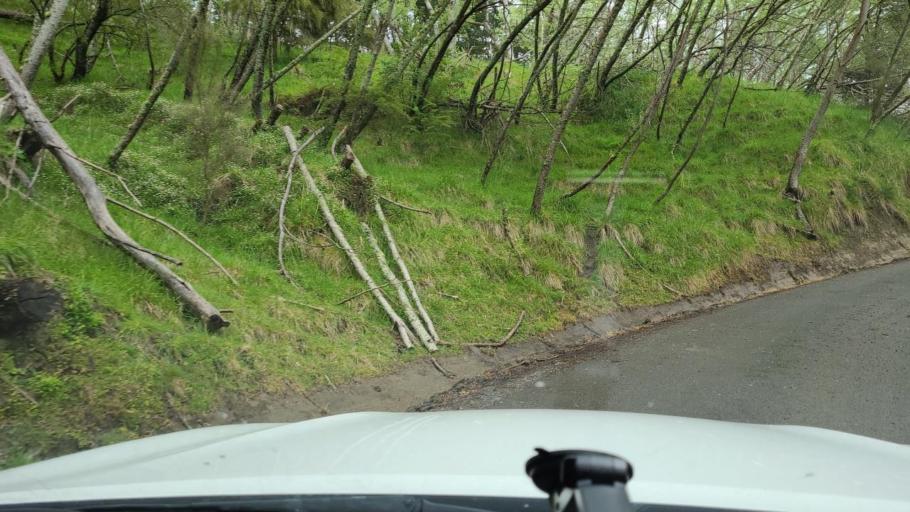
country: NZ
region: Gisborne
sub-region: Gisborne District
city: Gisborne
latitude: -38.4308
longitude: 177.7158
